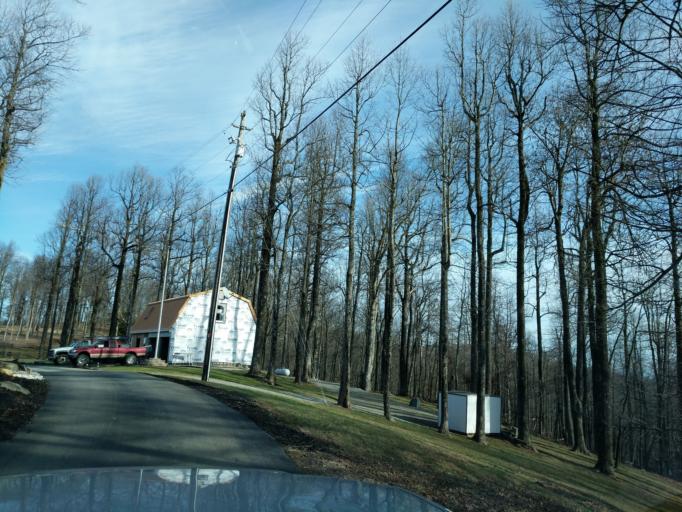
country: US
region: North Carolina
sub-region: Polk County
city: Columbus
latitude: 35.2763
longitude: -82.2293
